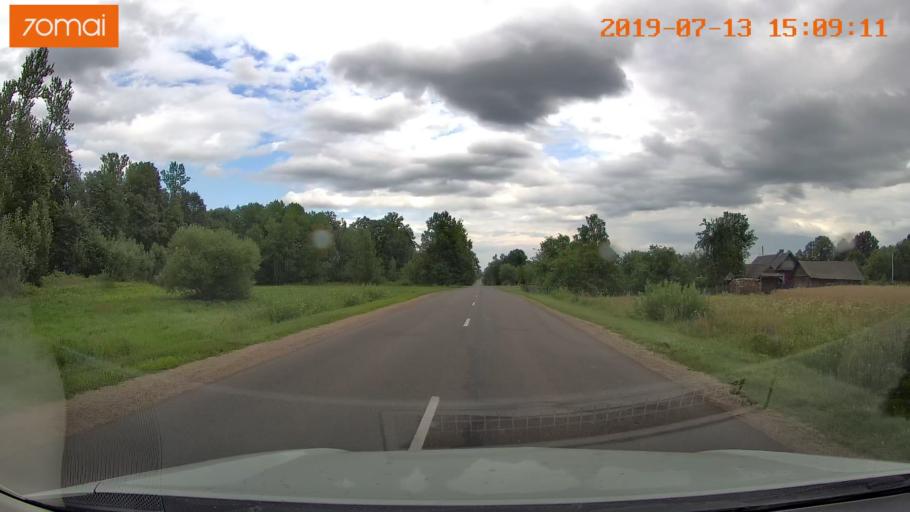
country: BY
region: Mogilev
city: Hlusha
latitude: 53.1738
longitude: 28.7581
